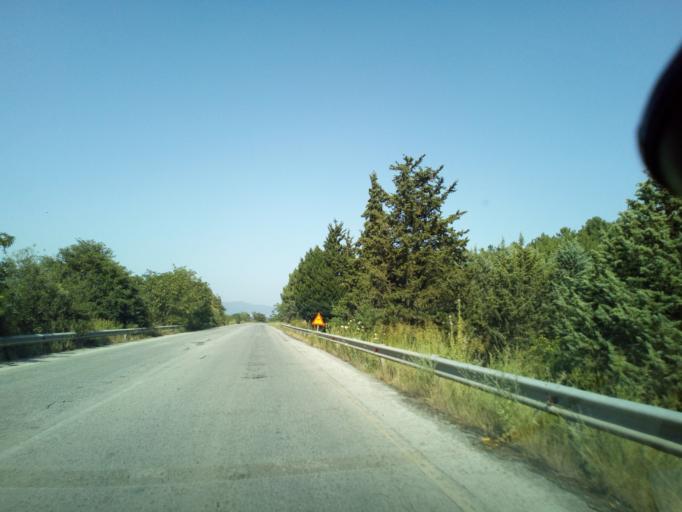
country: GR
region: Central Macedonia
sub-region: Nomos Thessalonikis
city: Nea Apollonia
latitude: 40.6605
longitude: 23.3705
